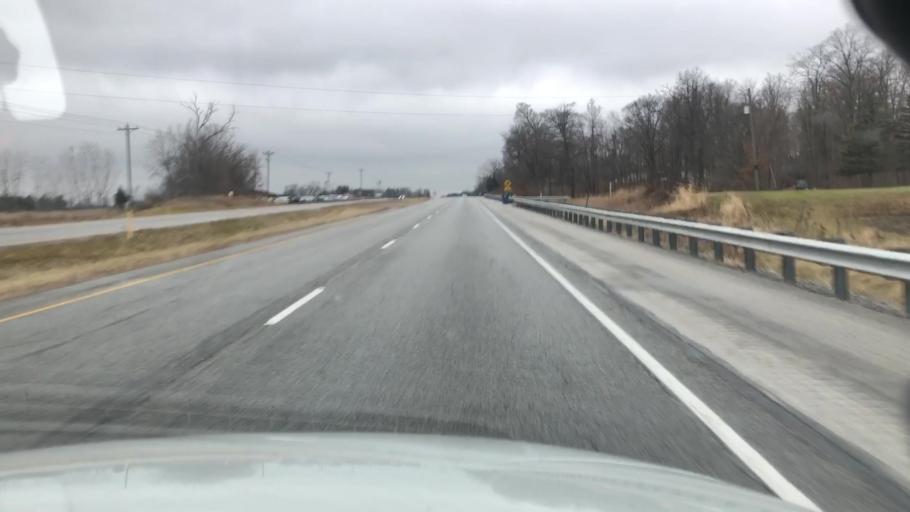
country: US
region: Indiana
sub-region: Whitley County
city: Columbia City
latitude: 41.1765
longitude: -85.5641
